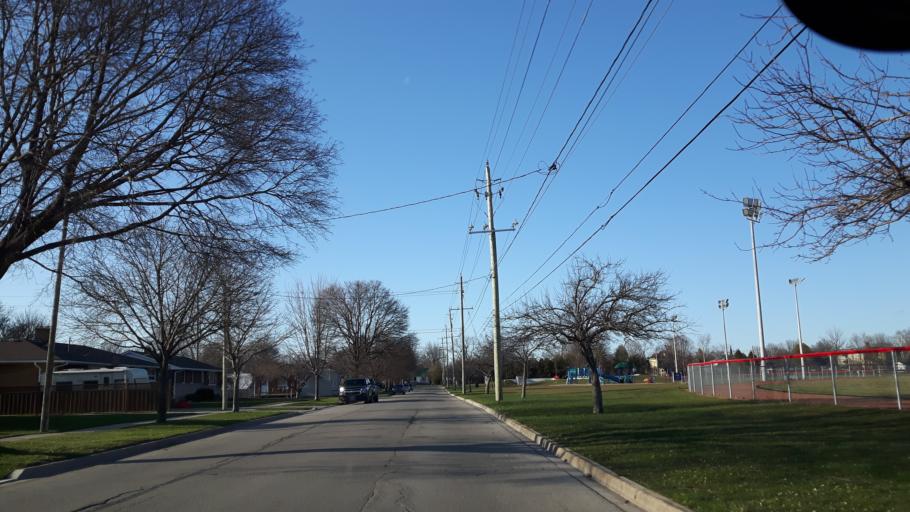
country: CA
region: Ontario
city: Goderich
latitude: 43.7365
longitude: -81.7163
